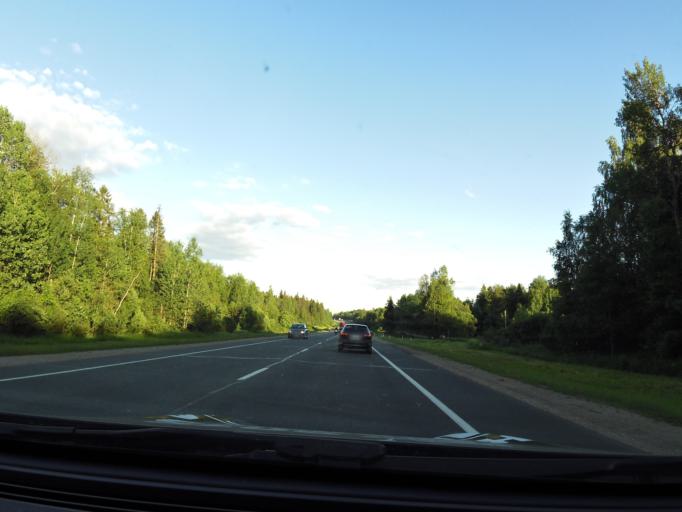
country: RU
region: Vologda
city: Vologda
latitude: 59.0867
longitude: 40.0071
